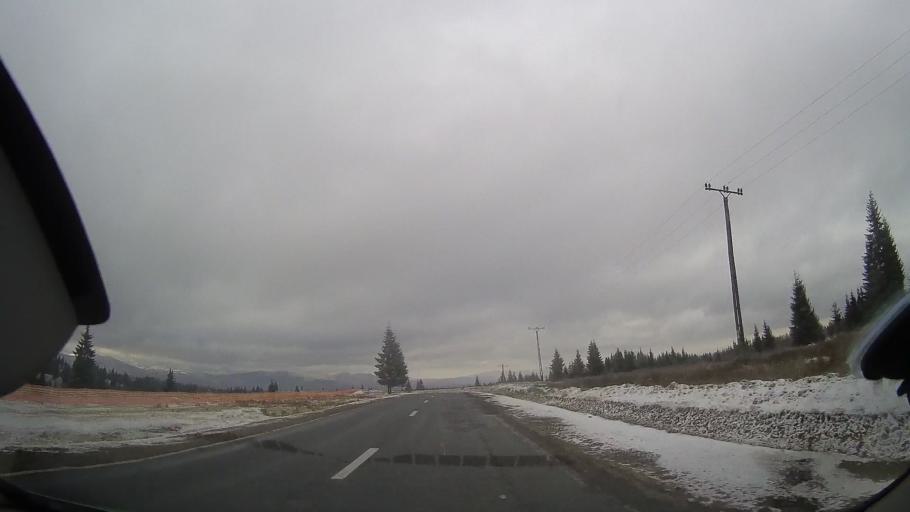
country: RO
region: Cluj
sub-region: Comuna Belis
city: Belis
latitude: 46.6970
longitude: 23.0374
